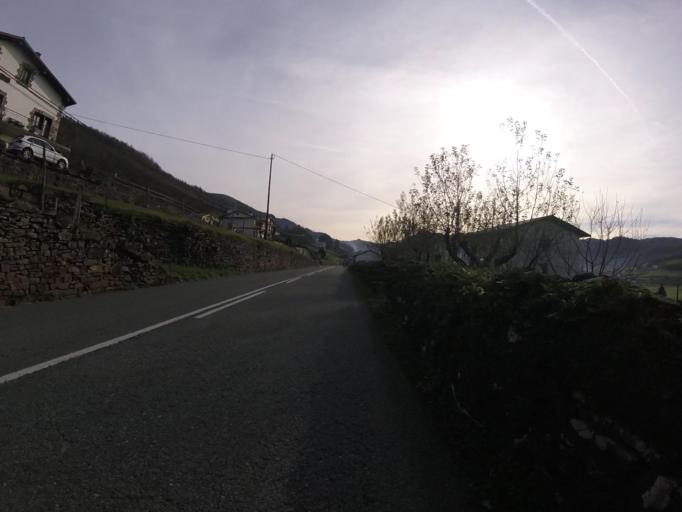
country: ES
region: Basque Country
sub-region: Provincia de Guipuzcoa
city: Berastegui
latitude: 43.1300
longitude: -1.9846
